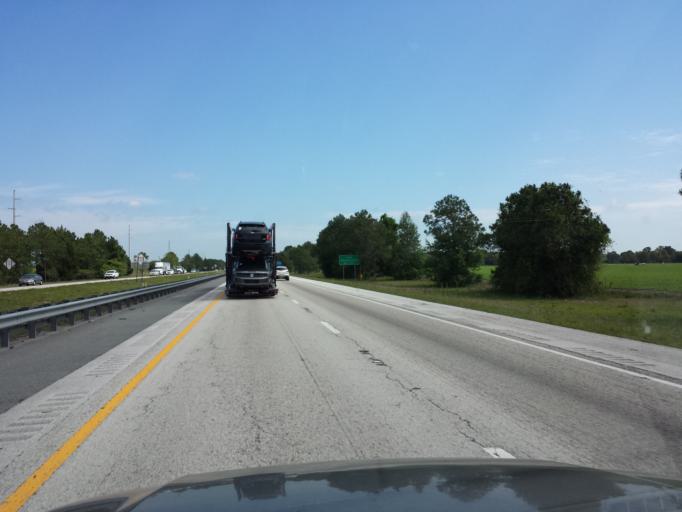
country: US
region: Florida
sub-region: Sumter County
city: Lake Panasoffkee
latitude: 28.7394
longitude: -82.1095
